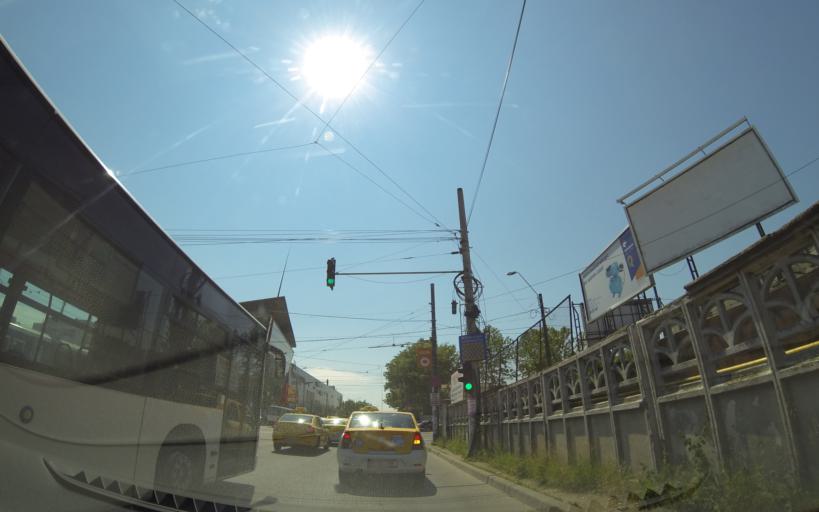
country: RO
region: Bucuresti
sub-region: Municipiul Bucuresti
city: Bucuresti
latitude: 44.4158
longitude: 26.0780
